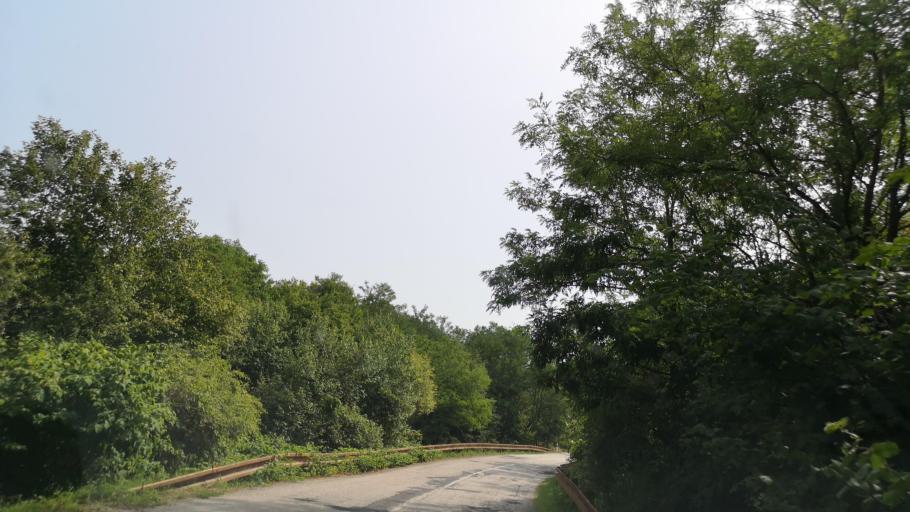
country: SK
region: Banskobystricky
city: Revuca
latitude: 48.5989
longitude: 20.1422
